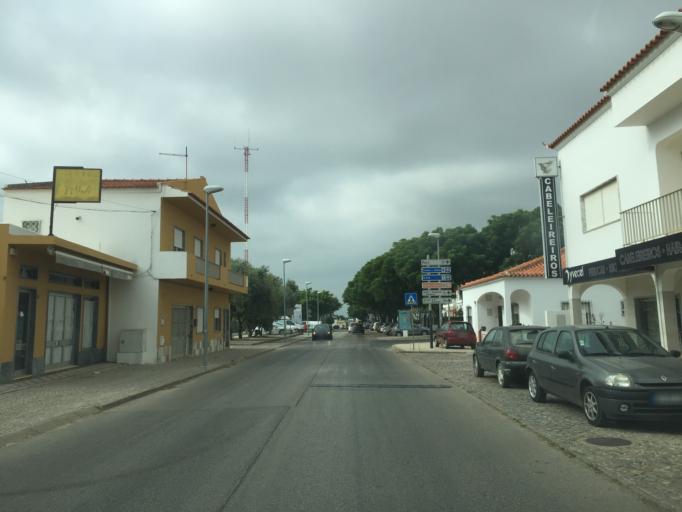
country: PT
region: Faro
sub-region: Loule
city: Almancil
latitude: 37.0890
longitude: -8.0290
